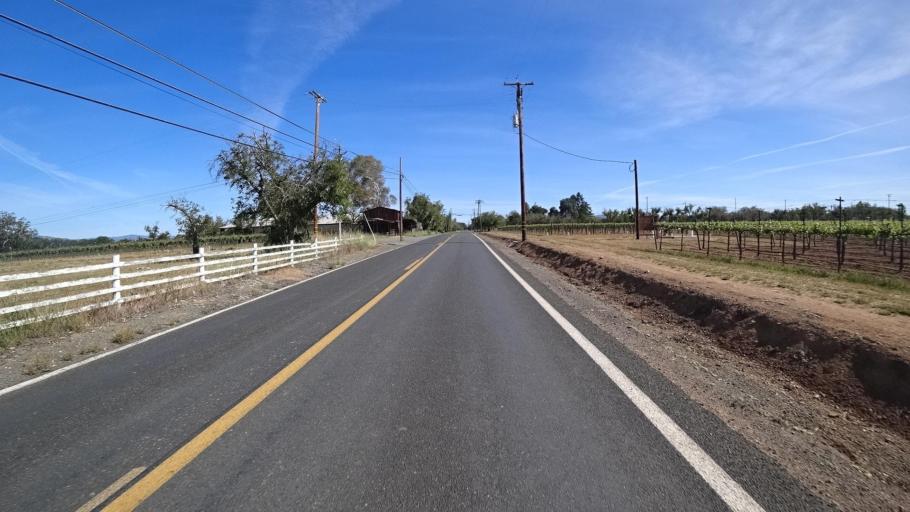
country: US
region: California
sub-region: Lake County
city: Kelseyville
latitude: 38.9739
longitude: -122.8571
